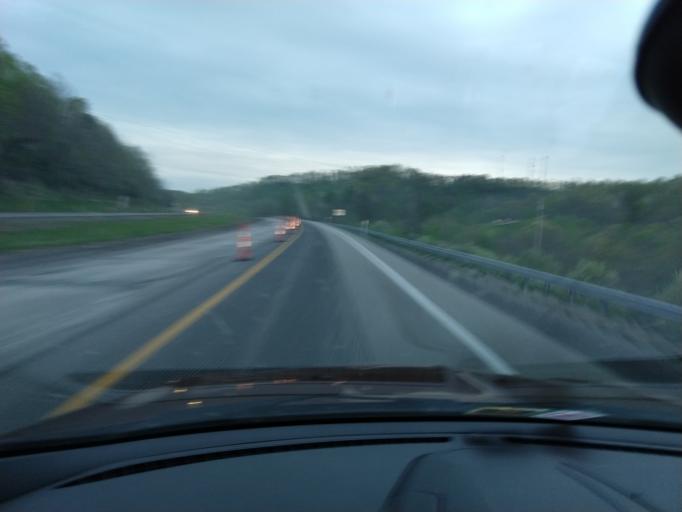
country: US
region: West Virginia
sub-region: Braxton County
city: Sutton
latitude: 38.7197
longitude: -80.6614
